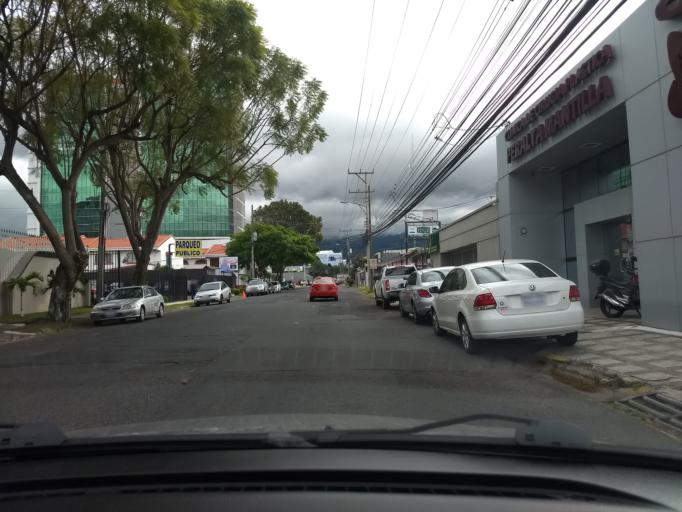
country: CR
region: San Jose
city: San Rafael
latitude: 9.9416
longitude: -84.1182
